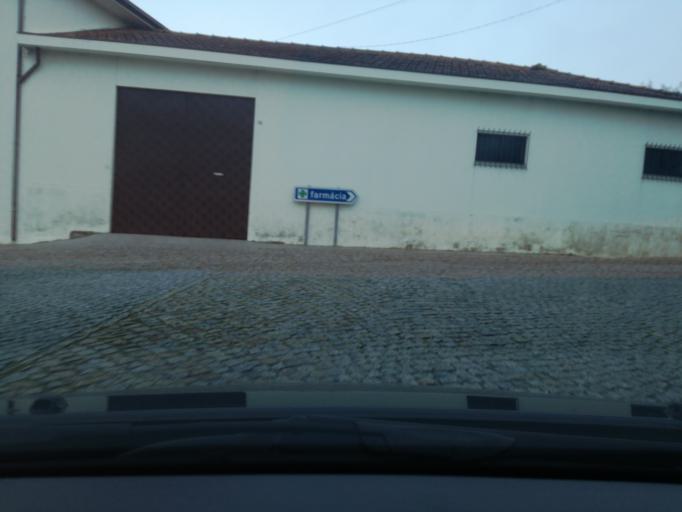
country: PT
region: Porto
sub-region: Maia
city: Gemunde
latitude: 41.2689
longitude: -8.6464
